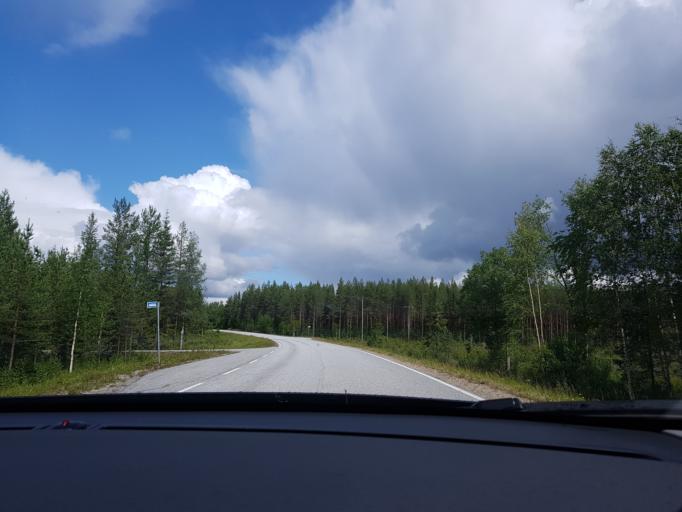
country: FI
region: Kainuu
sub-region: Kehys-Kainuu
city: Kuhmo
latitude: 64.4256
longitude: 29.4987
